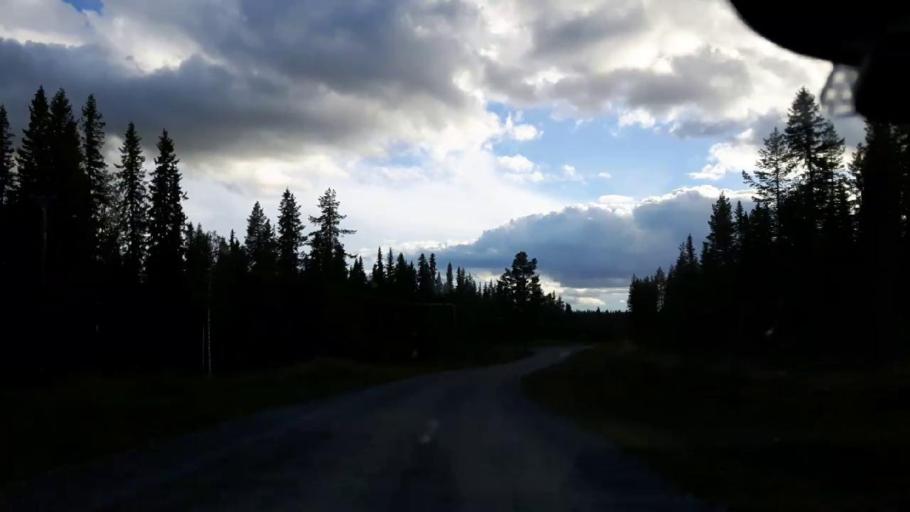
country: SE
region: Jaemtland
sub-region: Stroemsunds Kommun
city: Stroemsund
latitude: 63.3356
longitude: 15.5708
